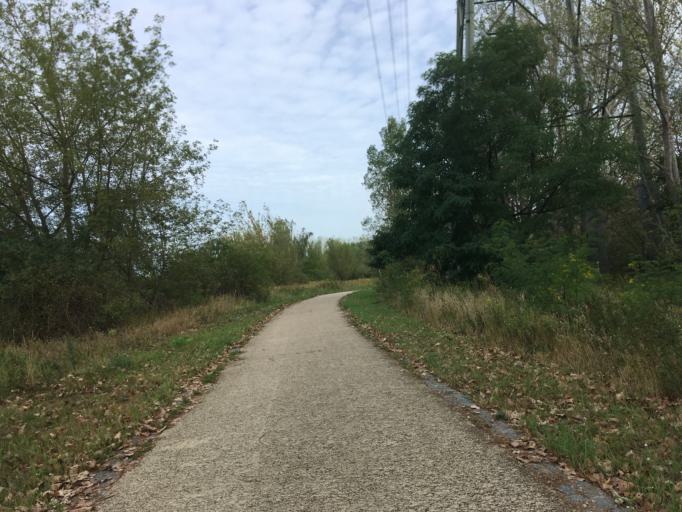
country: DE
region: Berlin
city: Falkenberg
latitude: 52.5550
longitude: 13.5416
